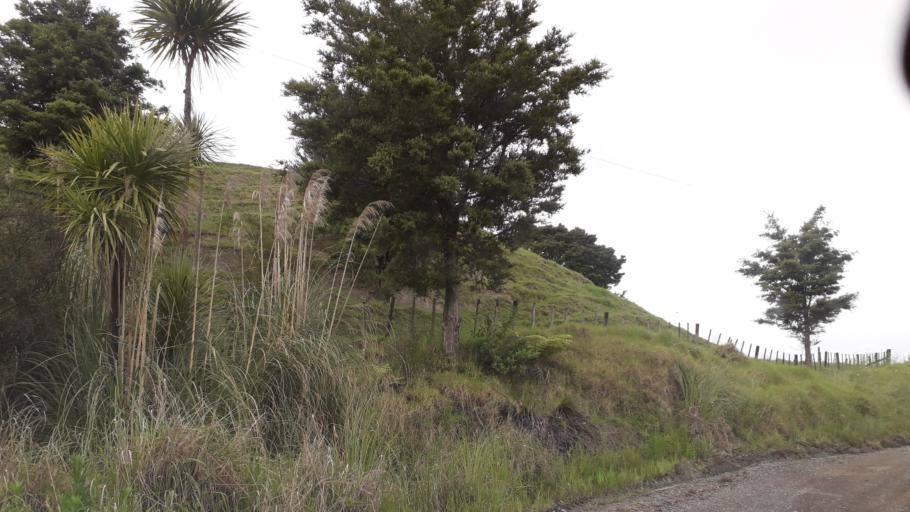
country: NZ
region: Northland
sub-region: Far North District
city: Waimate North
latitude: -35.3115
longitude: 173.5646
